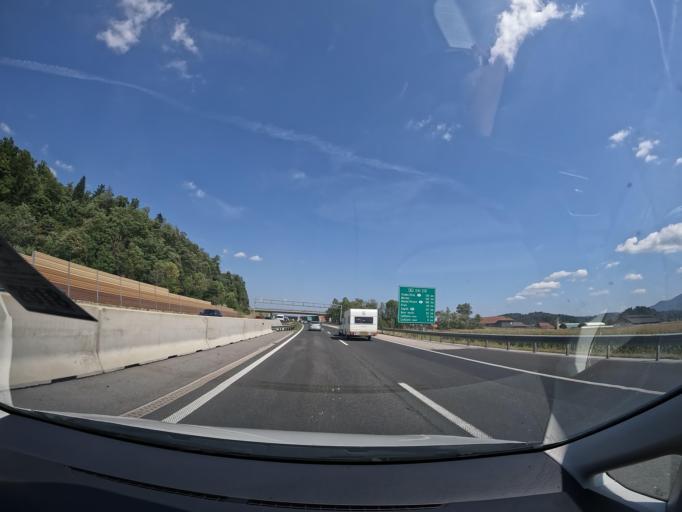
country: SI
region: Log-Dragomer
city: Log pri Brezovici
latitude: 46.0040
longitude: 14.3574
